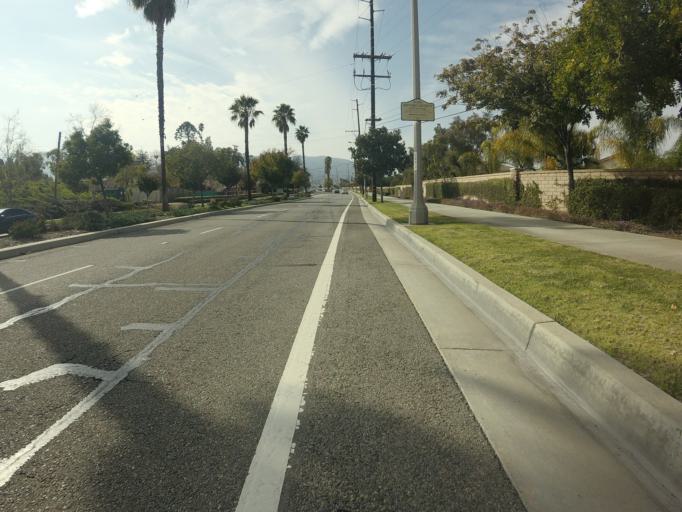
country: US
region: California
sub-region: Riverside County
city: Corona
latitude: 33.8452
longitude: -117.5751
